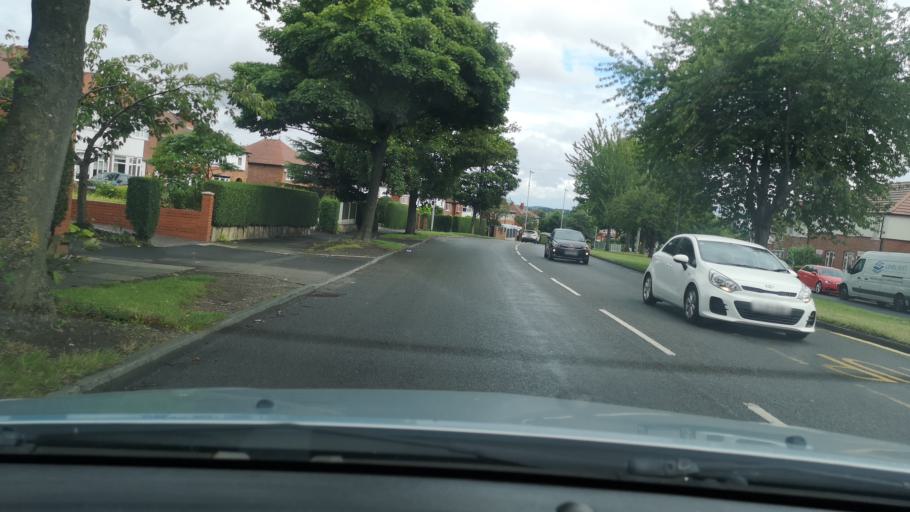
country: GB
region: England
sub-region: City and Borough of Wakefield
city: Horbury
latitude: 53.6794
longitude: -1.5399
